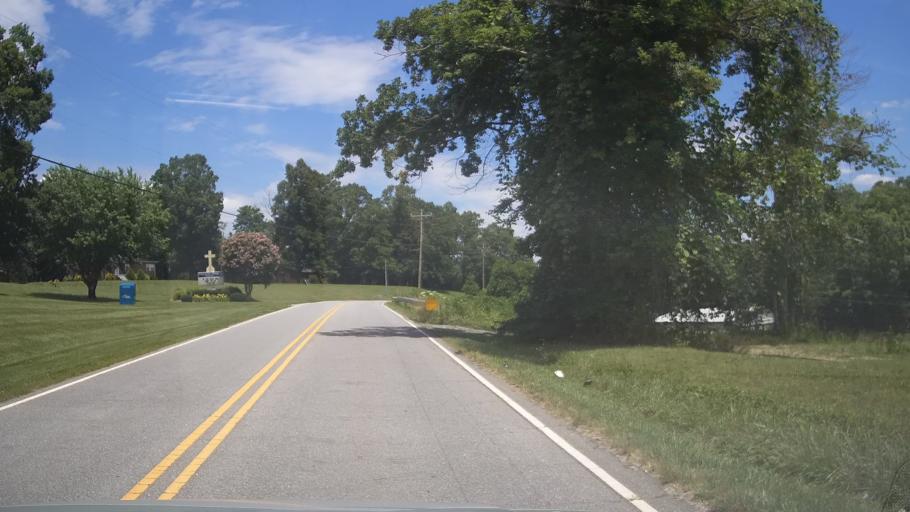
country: US
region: North Carolina
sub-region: Burke County
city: Glen Alpine
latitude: 35.6720
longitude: -81.7695
